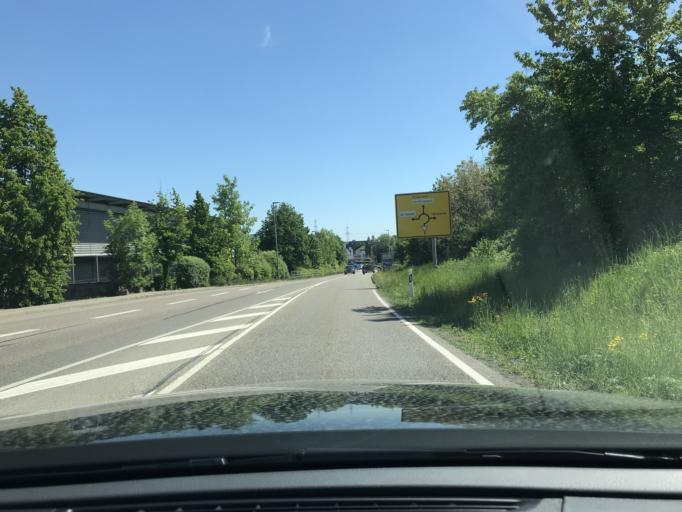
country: DE
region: Baden-Wuerttemberg
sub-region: Regierungsbezirk Stuttgart
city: Weinstadt-Endersbach
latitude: 48.8141
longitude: 9.3640
